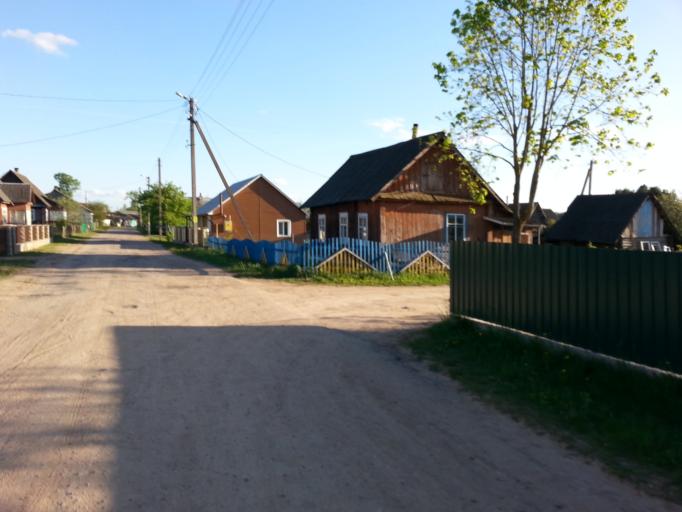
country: BY
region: Minsk
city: Narach
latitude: 54.9332
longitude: 26.6849
